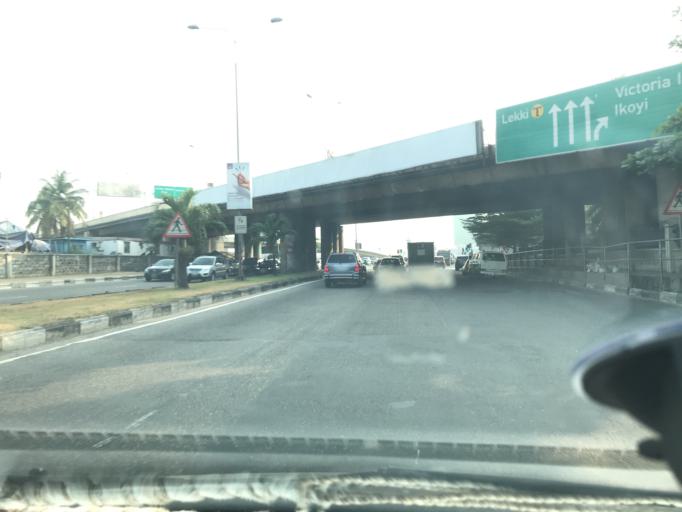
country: NG
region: Lagos
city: Ikoyi
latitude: 6.4385
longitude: 3.4245
